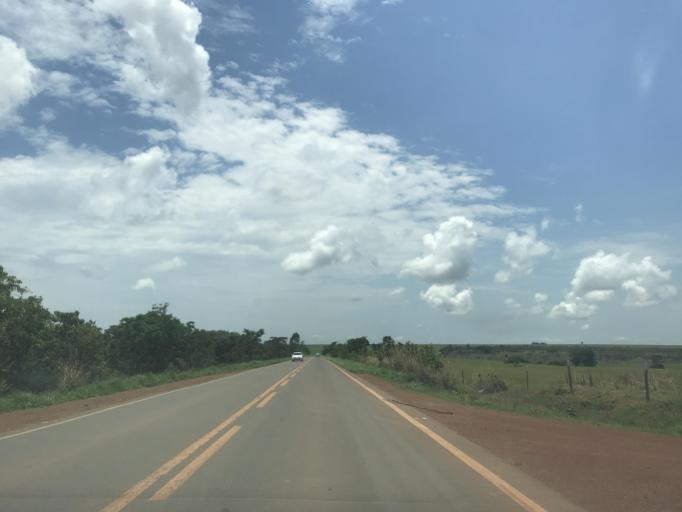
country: BR
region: Goias
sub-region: Luziania
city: Luziania
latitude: -16.4759
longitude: -48.2095
